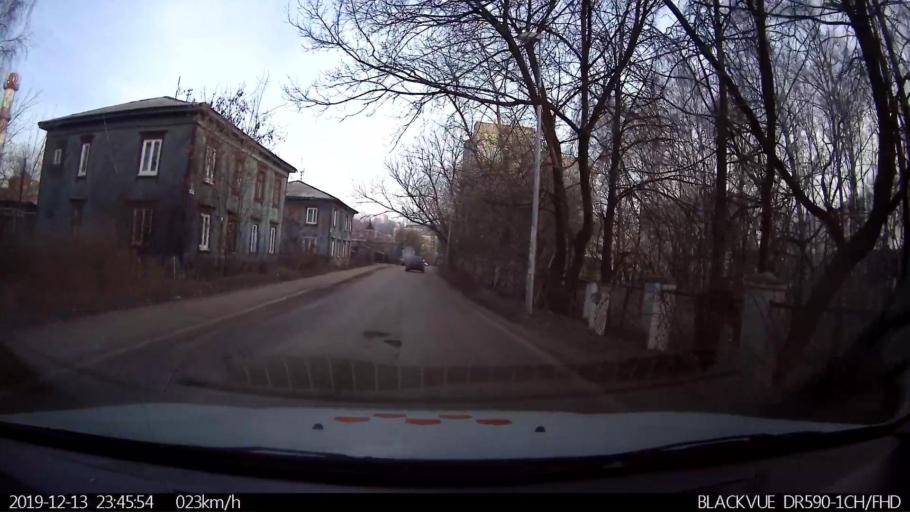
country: RU
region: Nizjnij Novgorod
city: Nizhniy Novgorod
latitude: 56.2931
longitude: 43.9443
